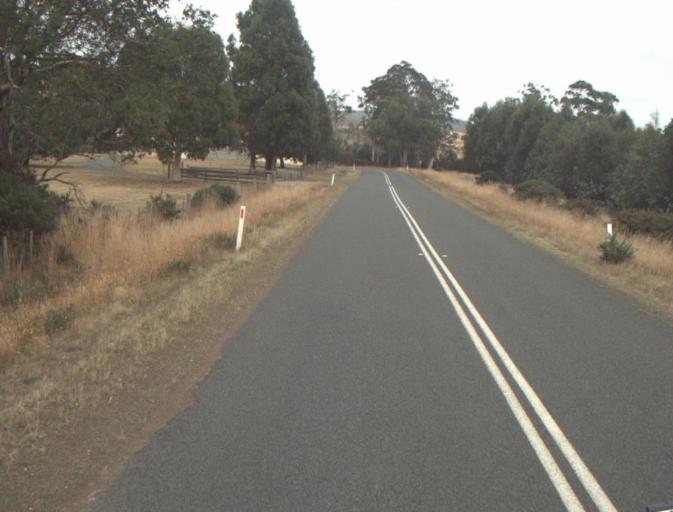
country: AU
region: Tasmania
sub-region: Northern Midlands
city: Evandale
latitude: -41.4815
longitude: 147.5064
